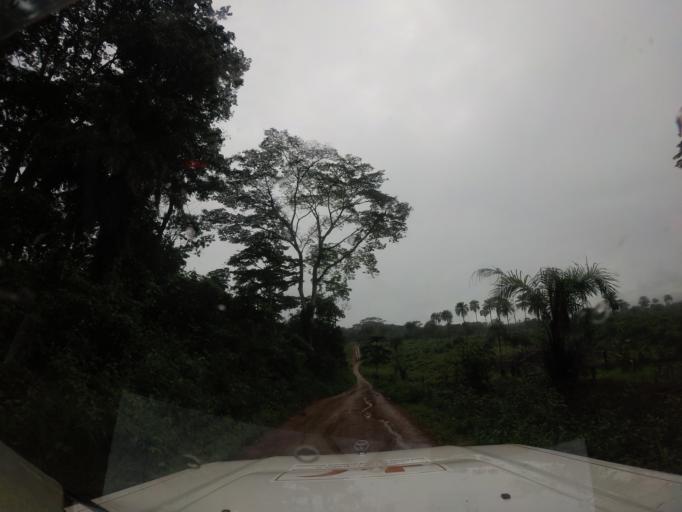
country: SL
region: Eastern Province
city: Kenema
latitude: 7.7483
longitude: -11.2054
